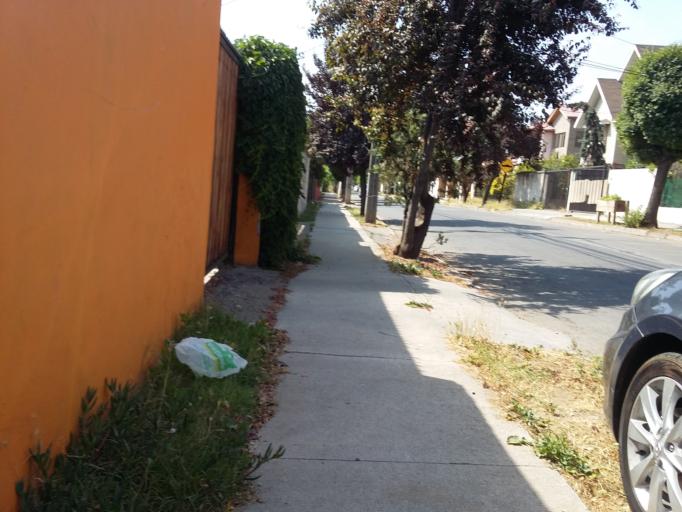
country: CL
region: Santiago Metropolitan
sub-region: Provincia de Santiago
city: La Pintana
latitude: -33.5384
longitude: -70.5877
